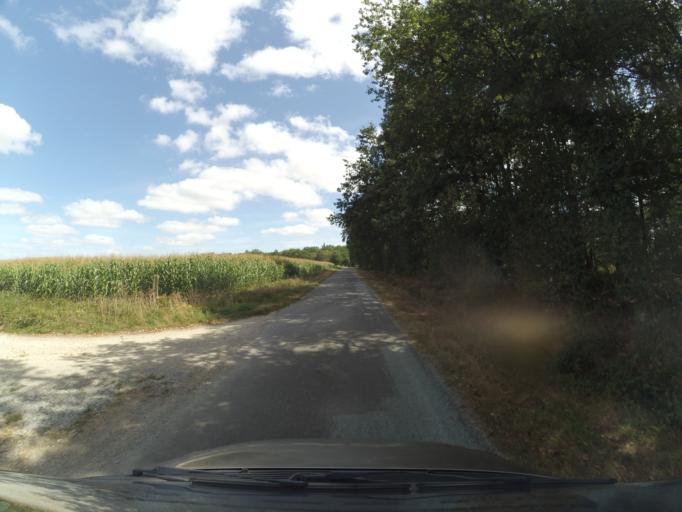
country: FR
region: Pays de la Loire
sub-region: Departement de la Loire-Atlantique
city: Remouille
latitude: 47.0412
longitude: -1.4074
